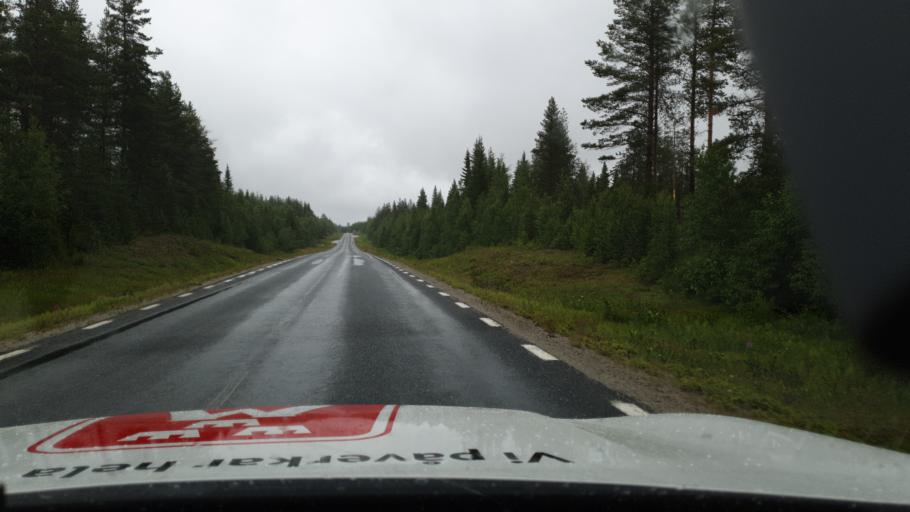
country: SE
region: Vaesterbotten
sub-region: Lycksele Kommun
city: Soderfors
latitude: 64.4868
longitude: 18.2784
